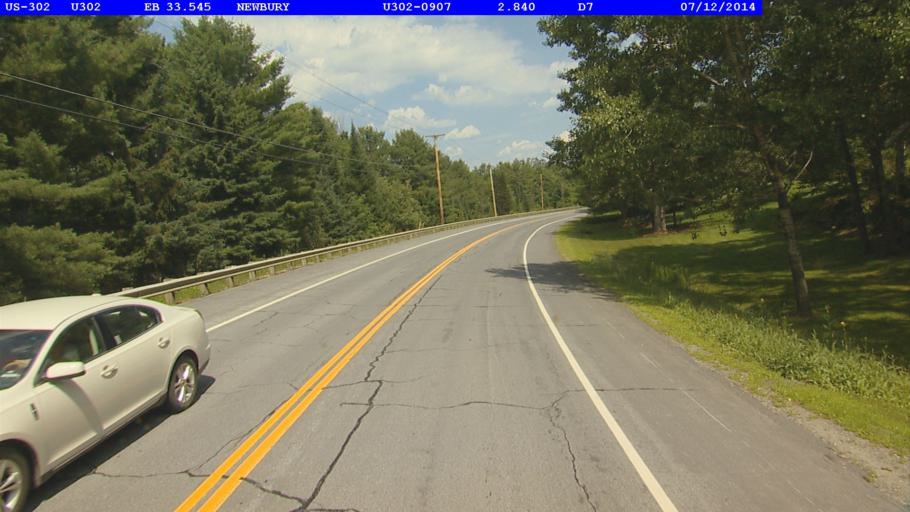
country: US
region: New Hampshire
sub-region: Grafton County
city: Woodsville
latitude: 44.1532
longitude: -72.0784
